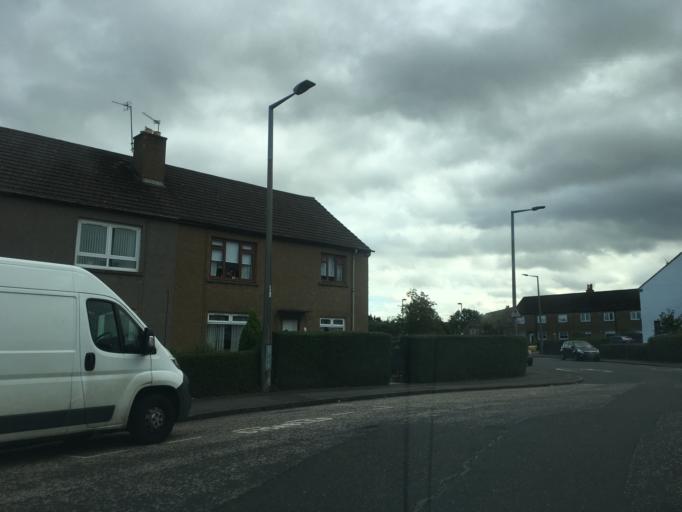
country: GB
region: Scotland
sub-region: Edinburgh
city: Edinburgh
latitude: 55.9641
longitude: -3.2488
